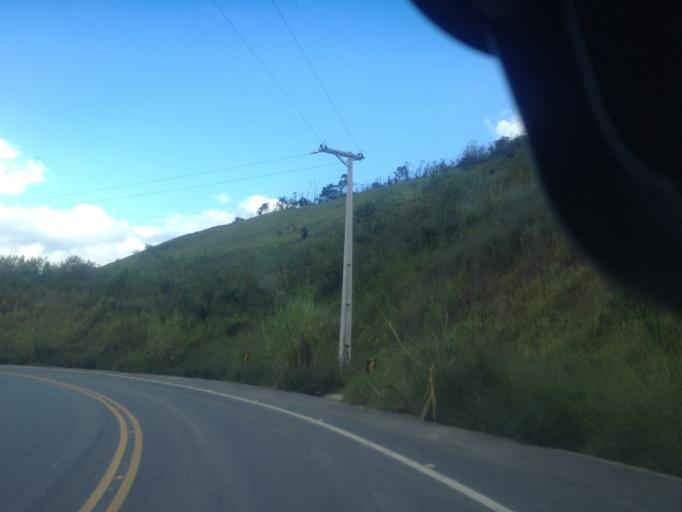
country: BR
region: Rio de Janeiro
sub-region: Quatis
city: Quatis
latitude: -22.2674
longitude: -44.2616
